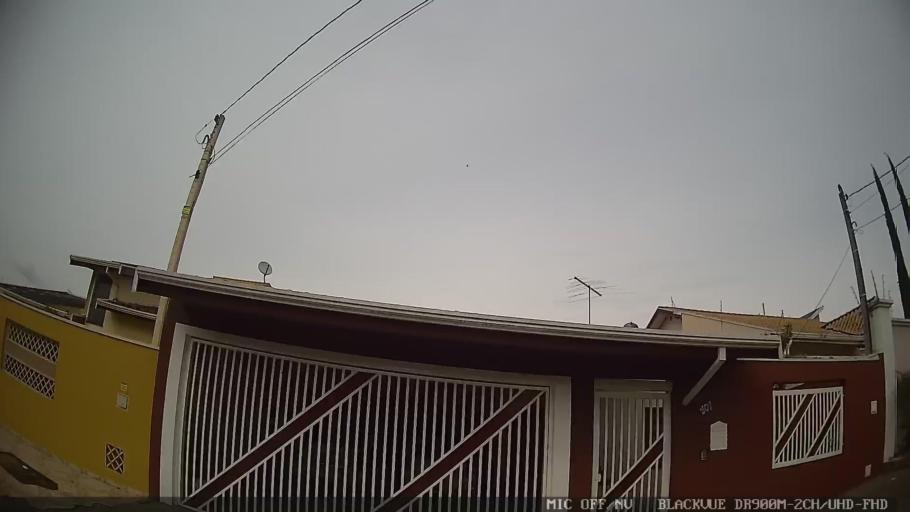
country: BR
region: Sao Paulo
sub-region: Indaiatuba
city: Indaiatuba
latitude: -23.0827
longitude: -47.2288
